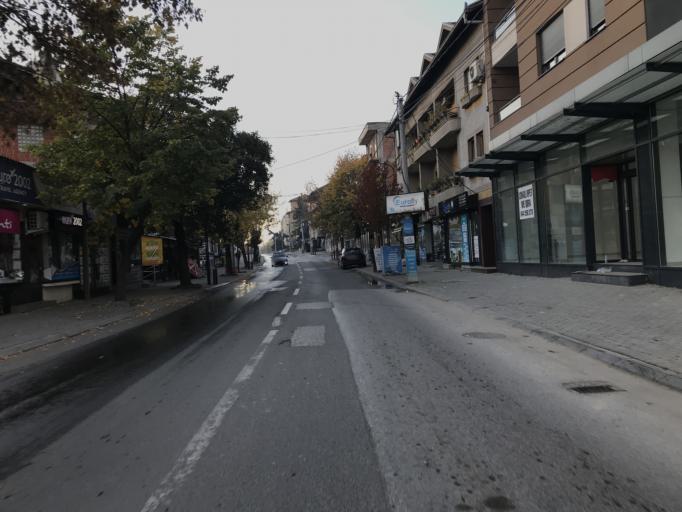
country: XK
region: Pec
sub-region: Komuna e Pejes
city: Peje
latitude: 42.6581
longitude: 20.2926
